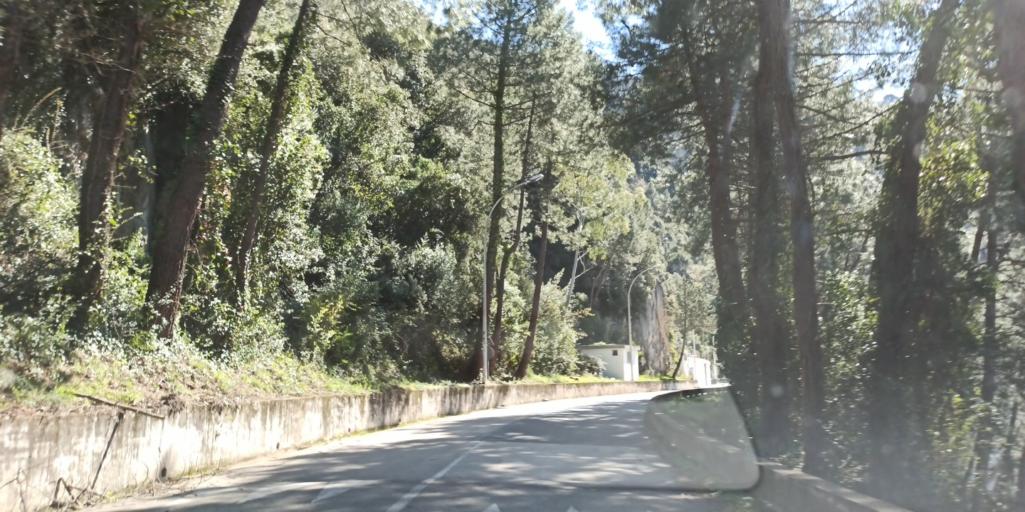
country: ES
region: Catalonia
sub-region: Provincia de Girona
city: Susqueda
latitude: 41.9806
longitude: 2.5298
